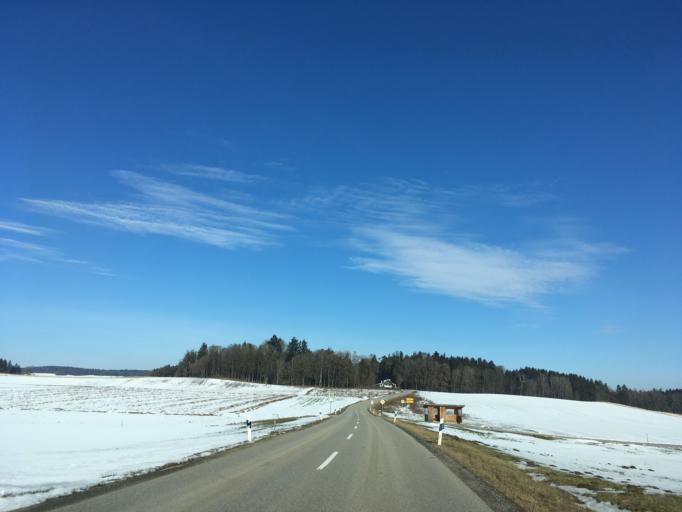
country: DE
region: Bavaria
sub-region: Upper Bavaria
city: Rechtmehring
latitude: 48.1024
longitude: 12.1609
